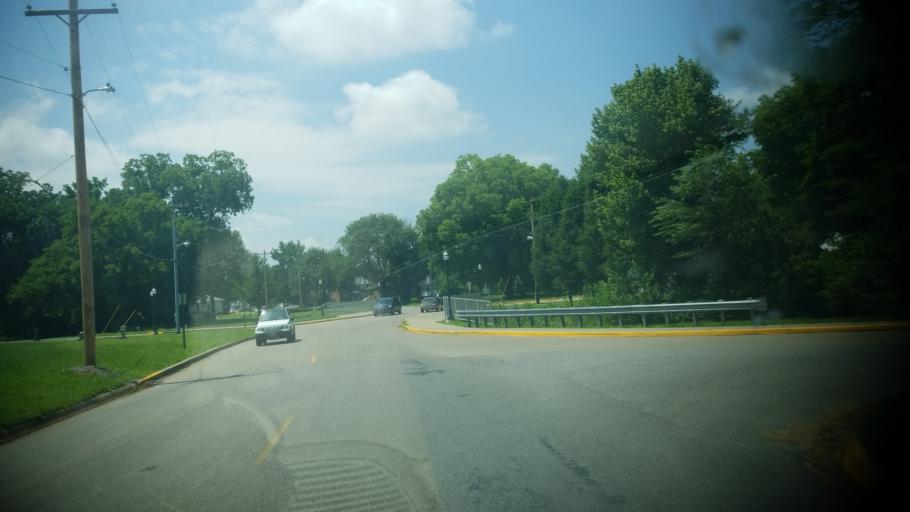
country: US
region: Illinois
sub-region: Wayne County
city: Fairfield
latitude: 38.3825
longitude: -88.3533
